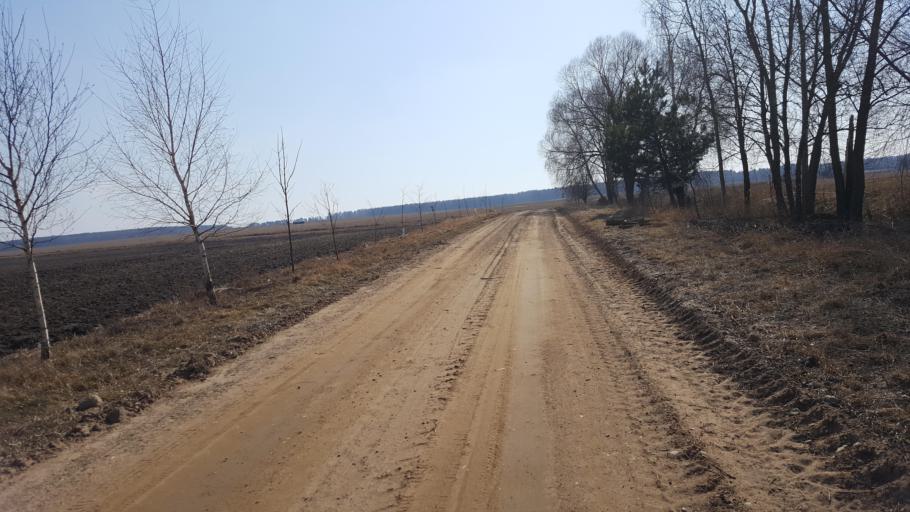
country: BY
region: Brest
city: Kamyanyets
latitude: 52.3600
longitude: 23.7629
